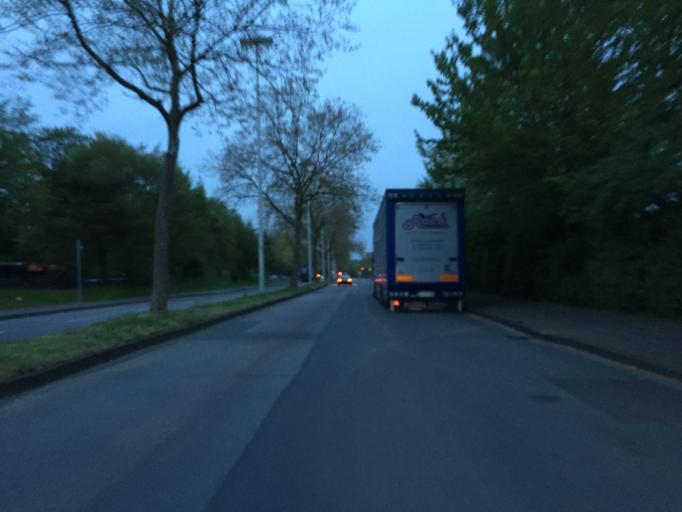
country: DE
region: North Rhine-Westphalia
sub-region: Regierungsbezirk Koln
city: Alfter
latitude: 50.7459
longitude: 7.0455
